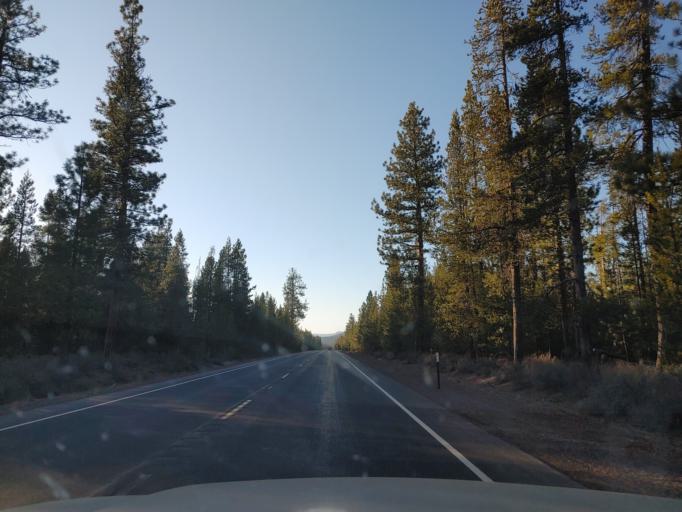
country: US
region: Oregon
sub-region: Deschutes County
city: La Pine
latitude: 43.3922
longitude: -121.8128
